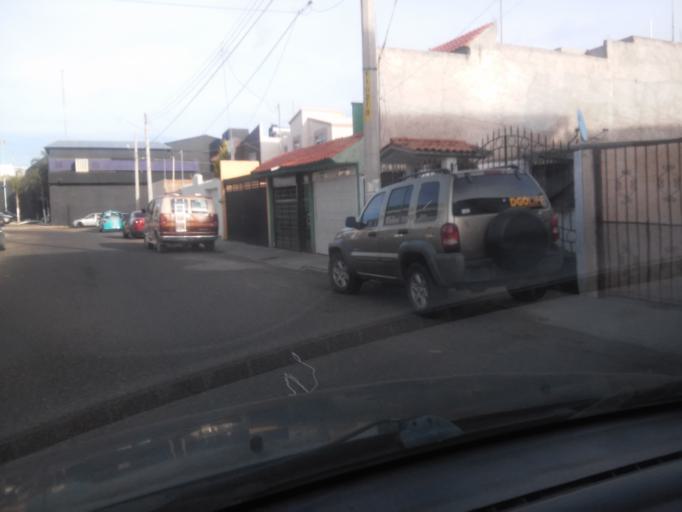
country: MX
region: Durango
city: Victoria de Durango
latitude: 24.0406
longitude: -104.6569
